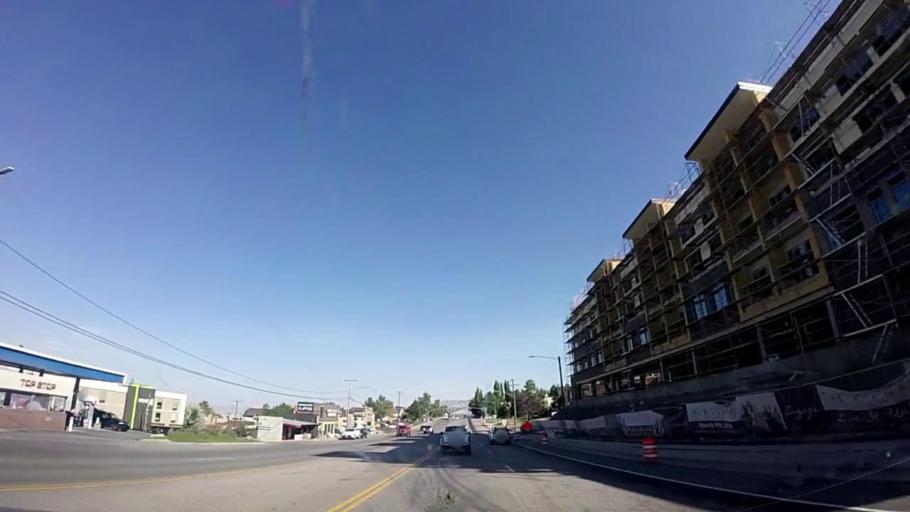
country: US
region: Utah
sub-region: Salt Lake County
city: Canyon Rim
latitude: 40.7199
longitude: -111.8104
